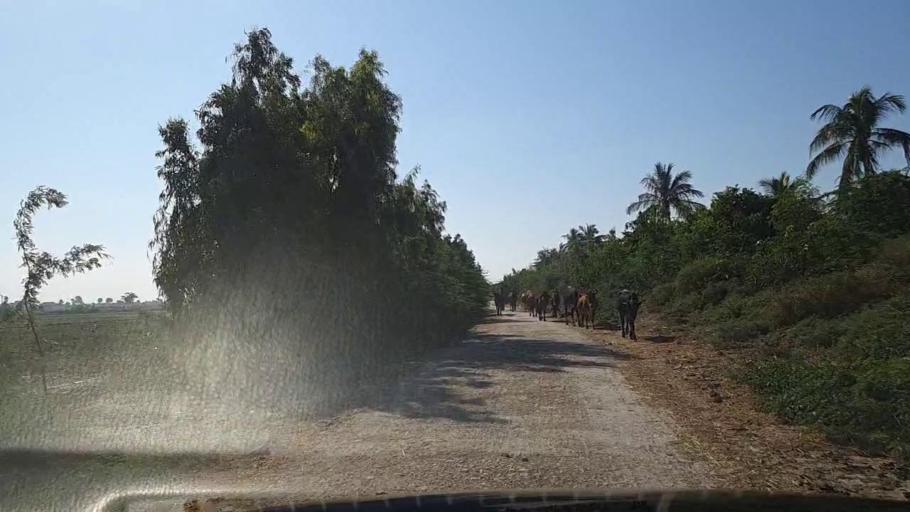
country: PK
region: Sindh
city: Thatta
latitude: 24.7113
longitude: 67.9187
